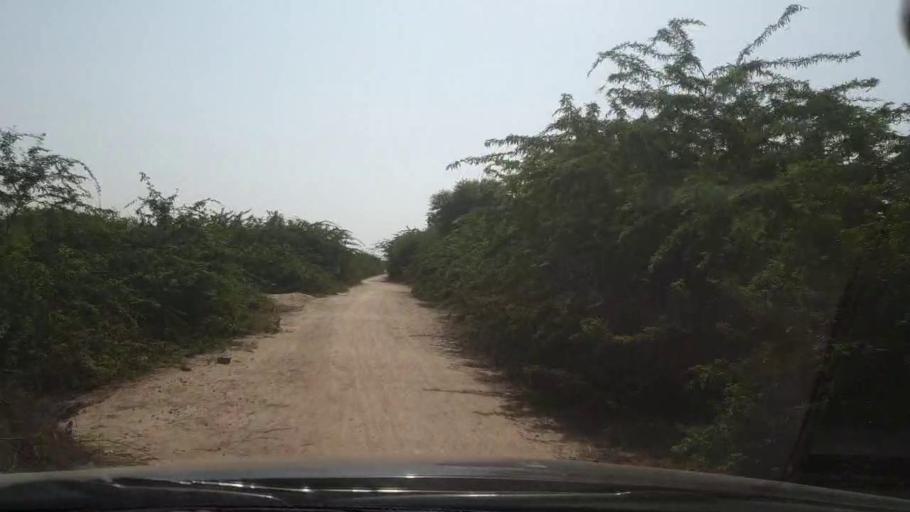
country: PK
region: Sindh
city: Naukot
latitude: 24.7989
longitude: 69.2498
